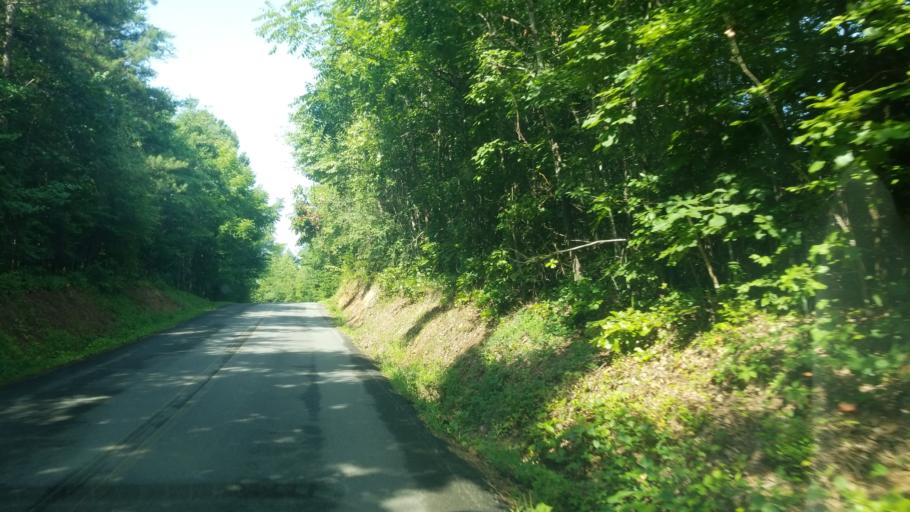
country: US
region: Tennessee
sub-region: Hamilton County
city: Collegedale
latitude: 35.0850
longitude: -84.9905
